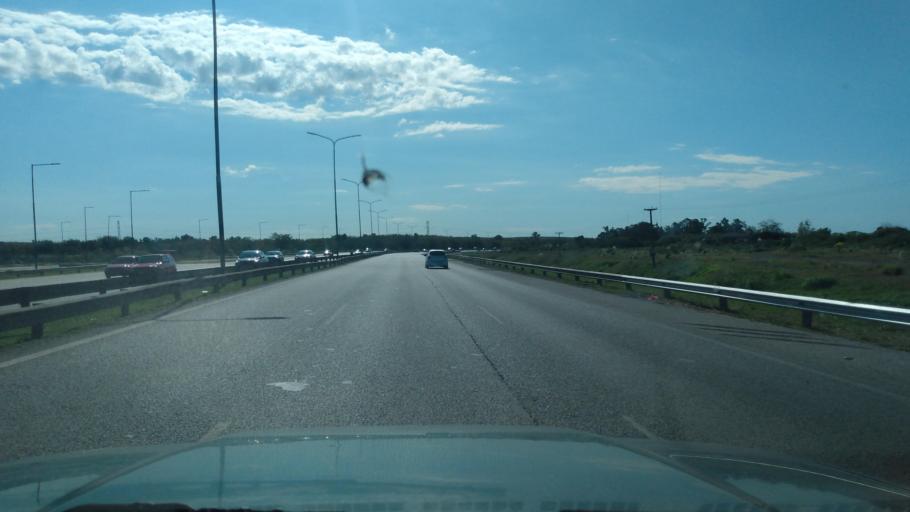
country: AR
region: Buenos Aires
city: Hurlingham
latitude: -34.5585
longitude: -58.6276
